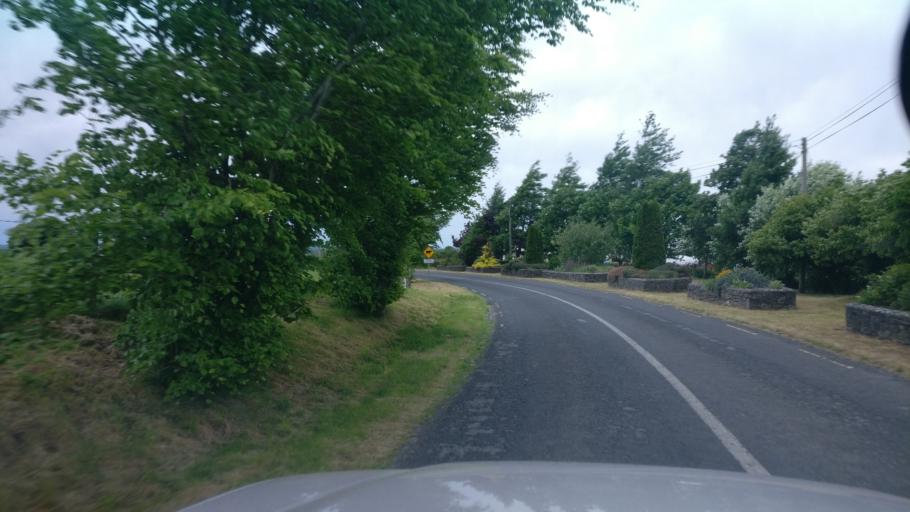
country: IE
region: Connaught
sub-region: County Galway
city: Portumna
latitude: 53.1131
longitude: -8.2785
